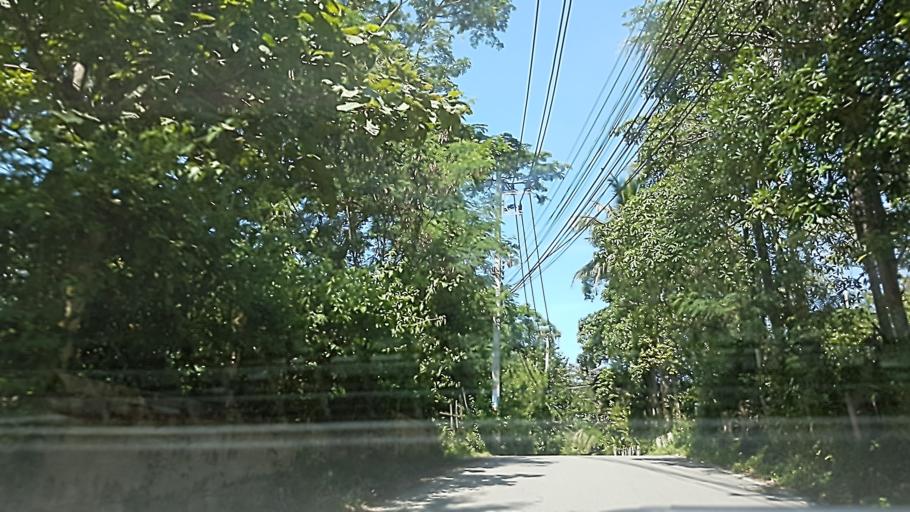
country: TH
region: Chiang Mai
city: Chiang Mai
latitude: 18.8231
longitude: 98.9564
